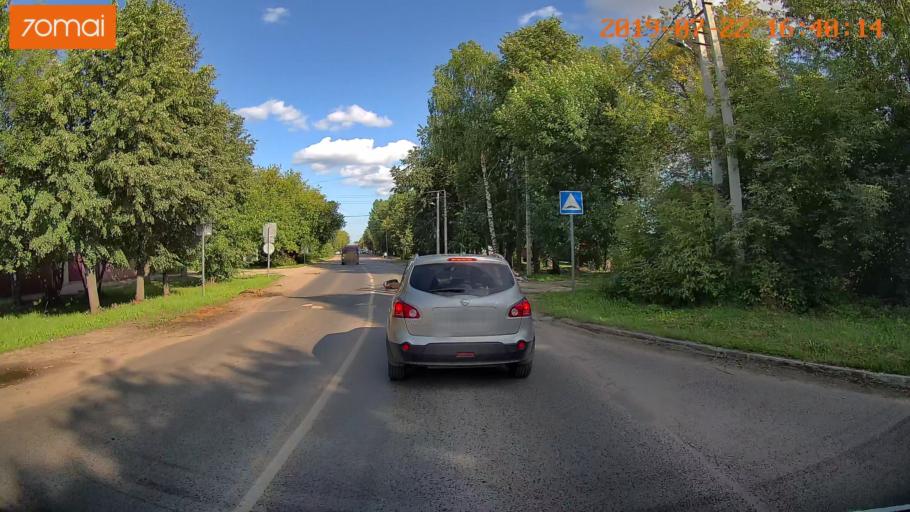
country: RU
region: Ivanovo
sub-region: Gorod Ivanovo
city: Ivanovo
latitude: 57.0239
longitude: 40.9562
